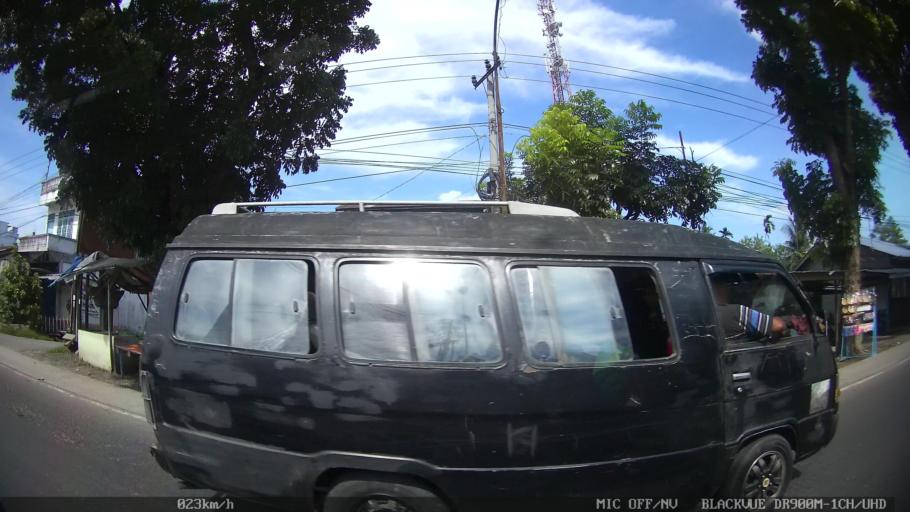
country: ID
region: North Sumatra
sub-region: Kabupaten Langkat
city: Stabat
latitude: 3.7029
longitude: 98.5064
